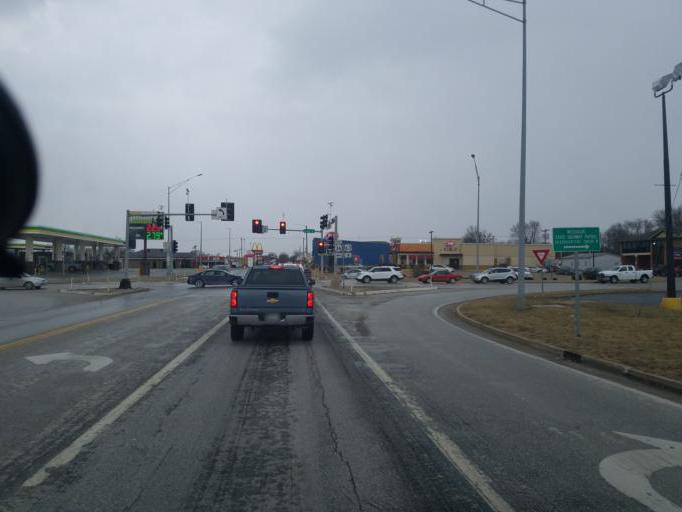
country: US
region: Missouri
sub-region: Macon County
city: Macon
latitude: 39.7526
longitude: -92.4679
